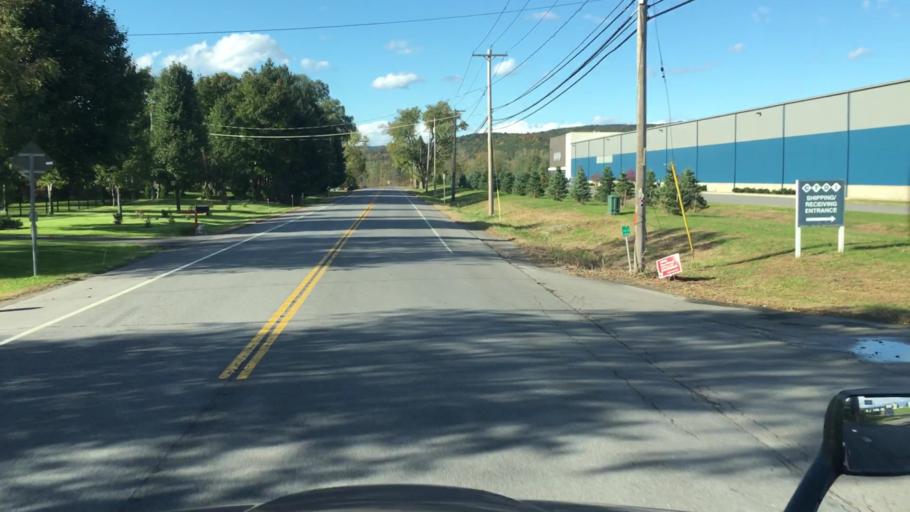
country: US
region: New York
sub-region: Schenectady County
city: Scotia
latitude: 42.8461
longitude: -73.9985
